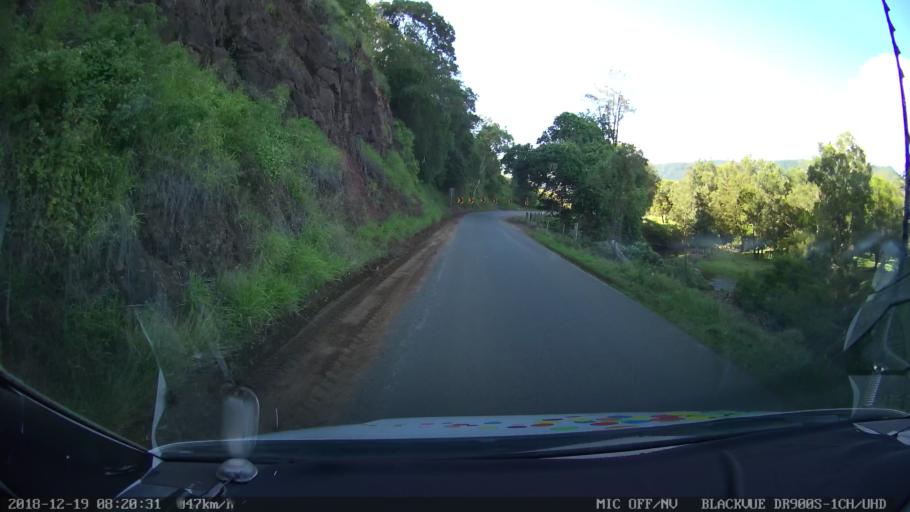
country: AU
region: New South Wales
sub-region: Kyogle
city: Kyogle
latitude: -28.2909
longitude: 152.9099
